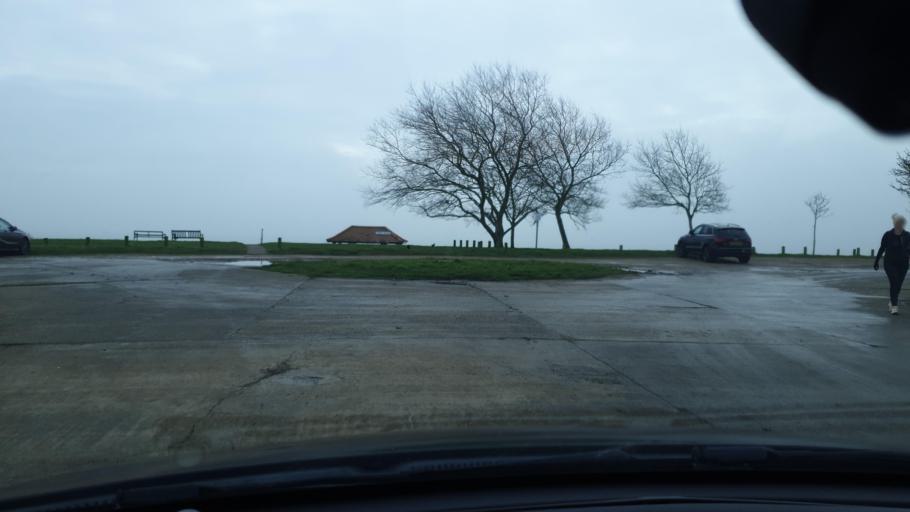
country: GB
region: England
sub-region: Essex
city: Walton-on-the-Naze
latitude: 51.8395
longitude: 1.2591
